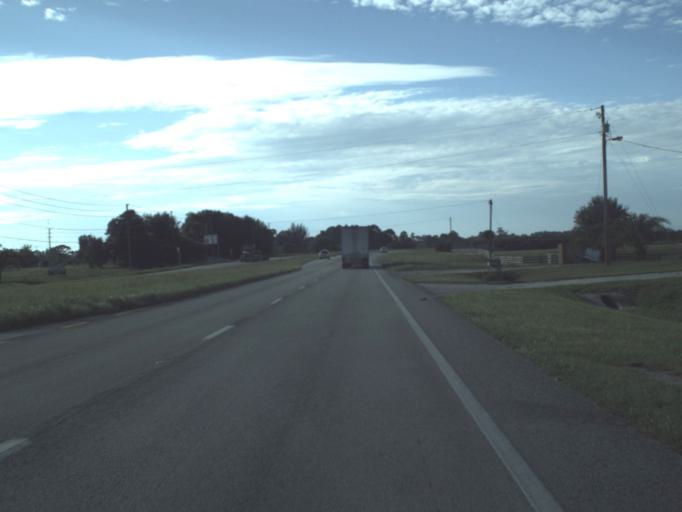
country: US
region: Florida
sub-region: Highlands County
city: Lake Placid
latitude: 27.2367
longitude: -81.3317
